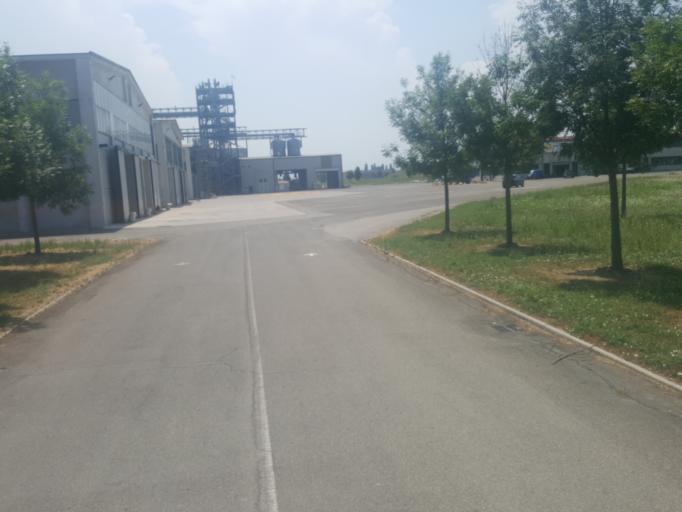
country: IT
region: Emilia-Romagna
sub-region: Provincia di Modena
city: Manzolino
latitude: 44.6049
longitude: 11.0892
